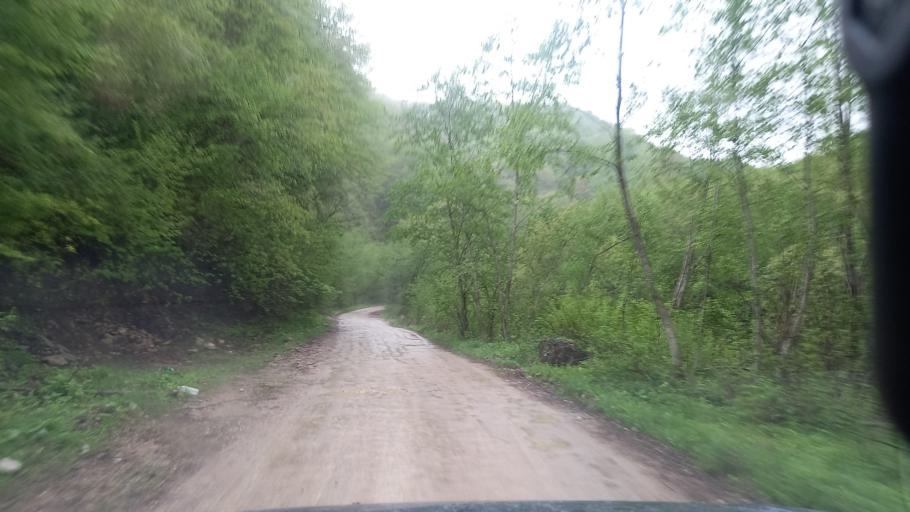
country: RU
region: Kabardino-Balkariya
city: Gundelen
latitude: 43.5802
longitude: 43.1089
